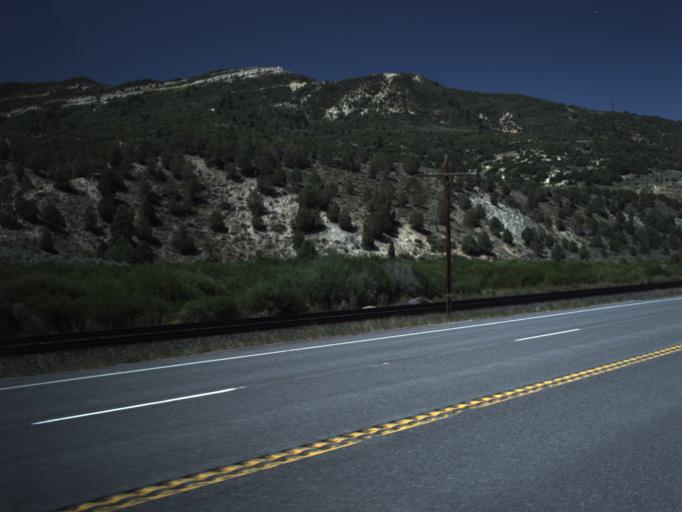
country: US
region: Utah
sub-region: Utah County
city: Mapleton
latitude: 39.9783
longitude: -111.3495
